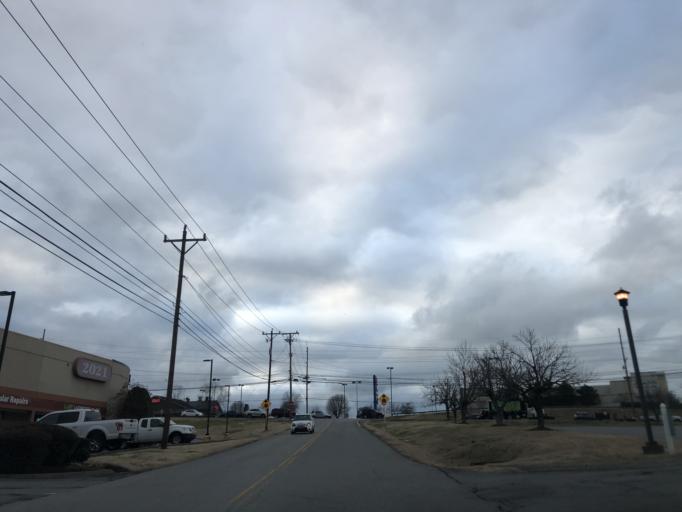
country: US
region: Tennessee
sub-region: Davidson County
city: Goodlettsville
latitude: 36.3015
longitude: -86.6917
